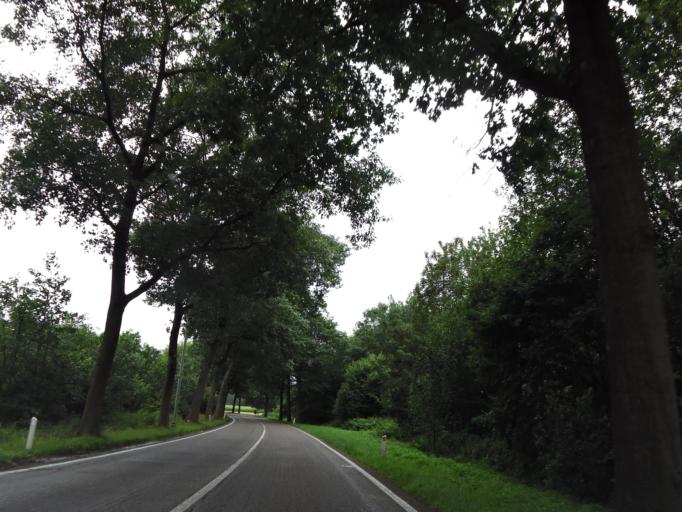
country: BE
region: Flanders
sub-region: Provincie Limburg
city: Bree
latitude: 51.0935
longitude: 5.5977
